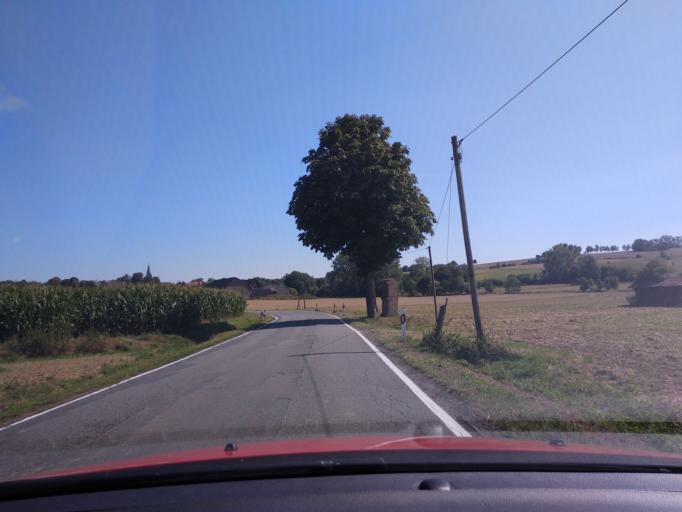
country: DE
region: North Rhine-Westphalia
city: Brakel
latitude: 51.6436
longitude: 9.1803
